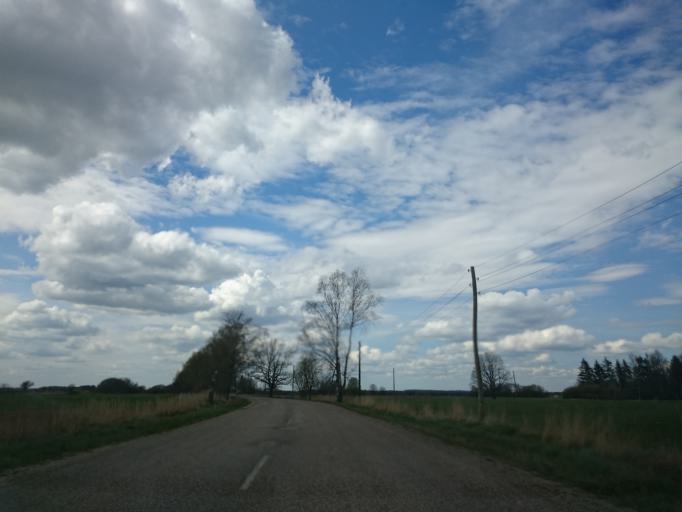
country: LV
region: Talsu Rajons
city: Sabile
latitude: 56.9493
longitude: 22.3637
